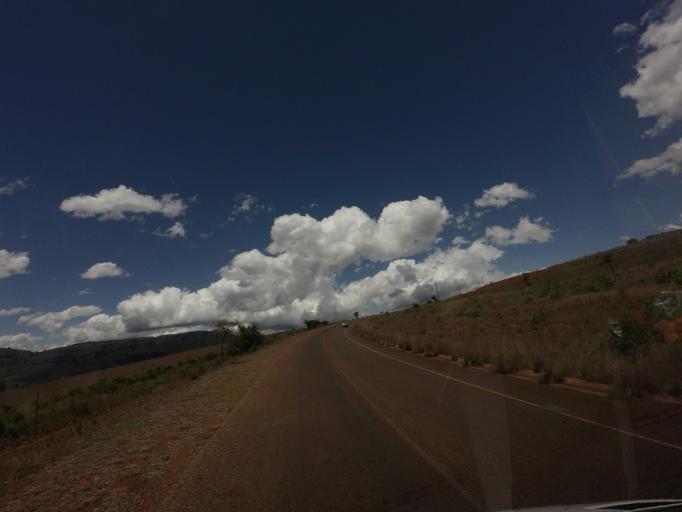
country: ZA
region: Limpopo
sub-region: Mopani District Municipality
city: Hoedspruit
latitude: -24.6074
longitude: 30.8101
